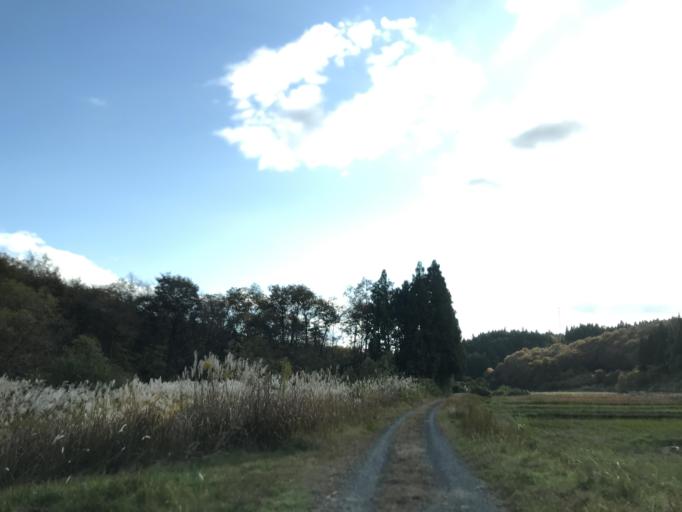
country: JP
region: Iwate
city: Ichinoseki
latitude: 38.8720
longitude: 141.1389
